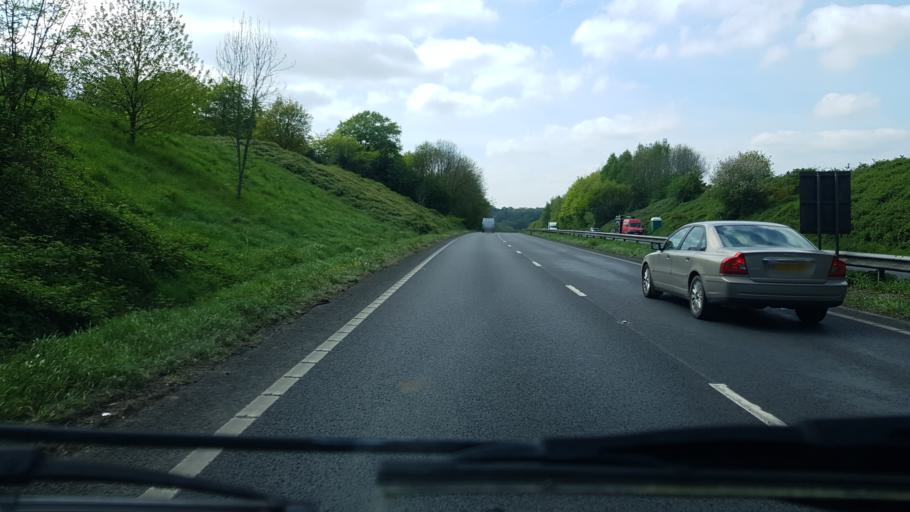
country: GB
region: England
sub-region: Kent
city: Pembury
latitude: 51.1388
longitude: 0.3281
